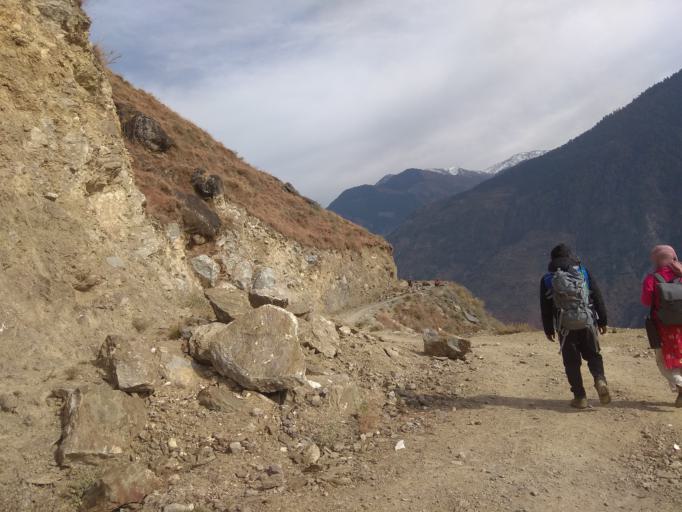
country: NP
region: Mid Western
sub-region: Bheri Zone
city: Dailekh
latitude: 29.2460
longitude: 81.6666
